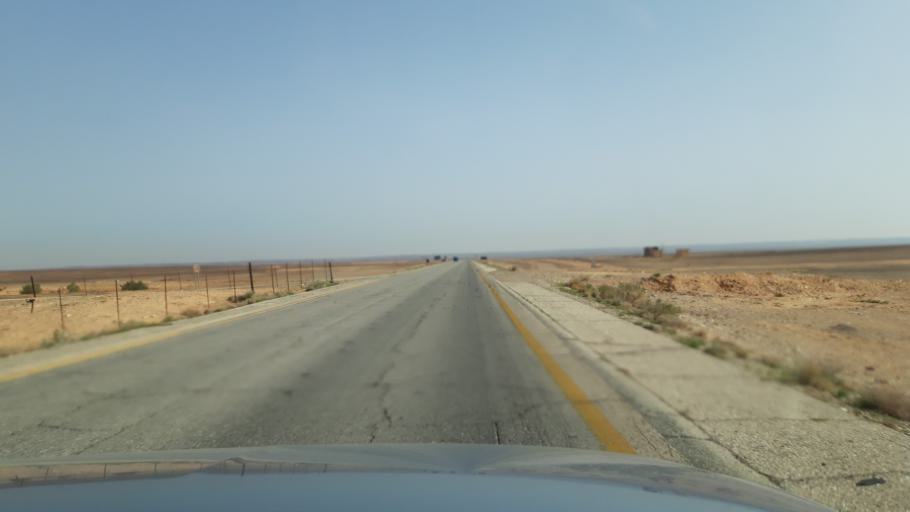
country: JO
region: Amman
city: Al Azraq ash Shamali
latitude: 31.8016
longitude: 36.5898
